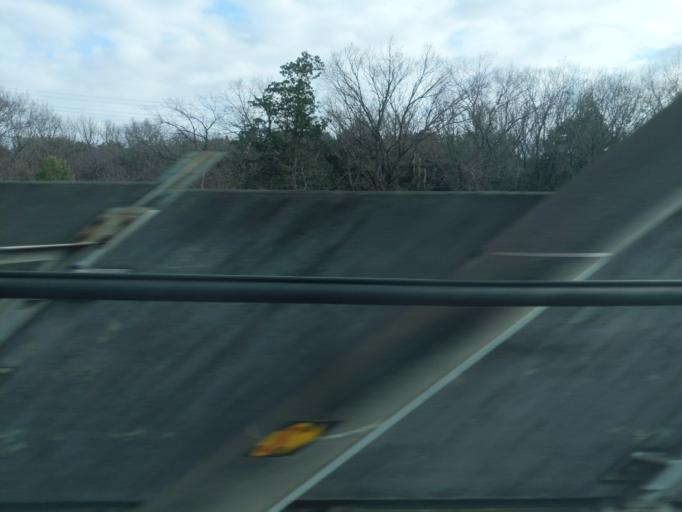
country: JP
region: Tochigi
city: Oyama
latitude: 36.3400
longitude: 139.8219
